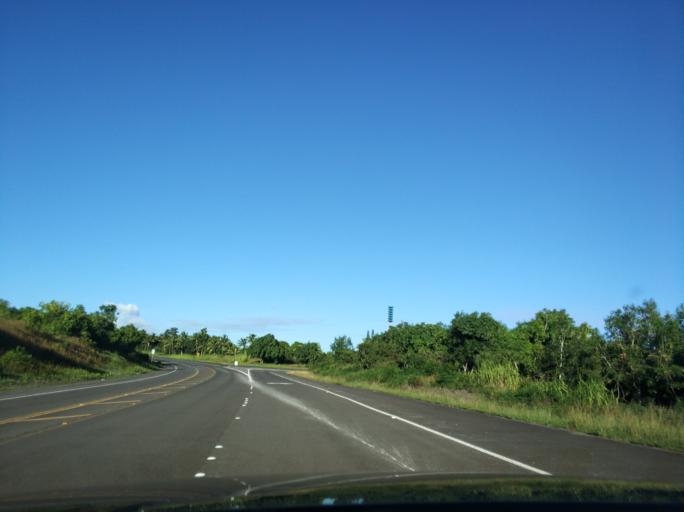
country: US
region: Hawaii
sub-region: Hawaii County
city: Leilani Estates
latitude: 19.3671
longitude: -154.9669
